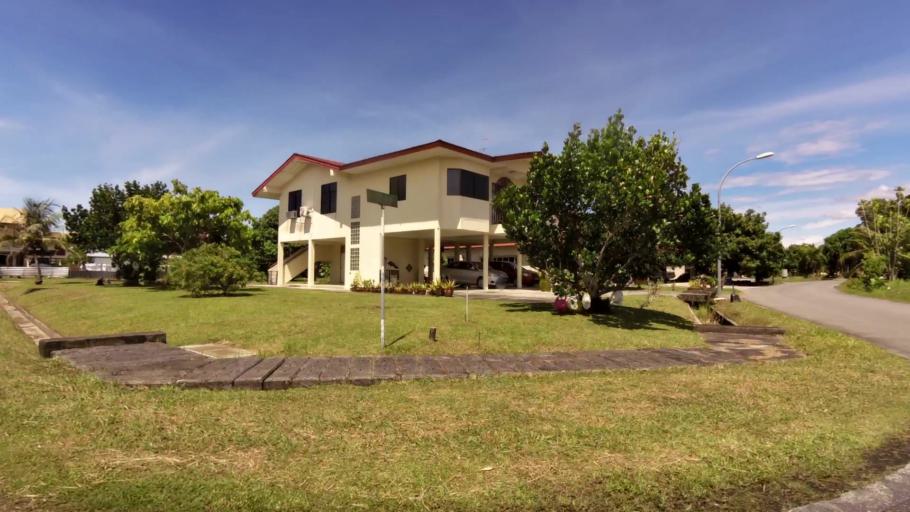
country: BN
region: Belait
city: Kuala Belait
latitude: 4.5874
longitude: 114.2247
